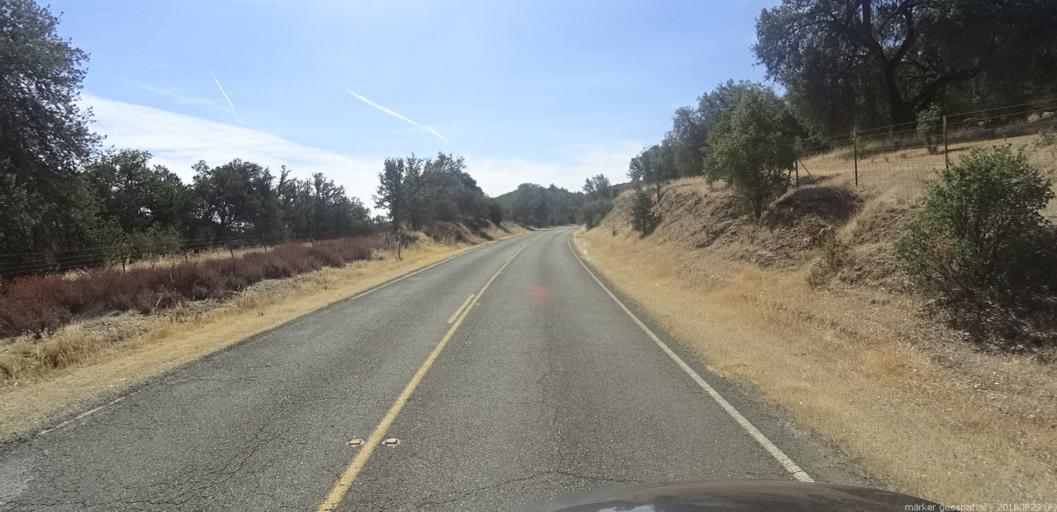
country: US
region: California
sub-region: San Luis Obispo County
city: Lake Nacimiento
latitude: 35.8947
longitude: -121.0848
